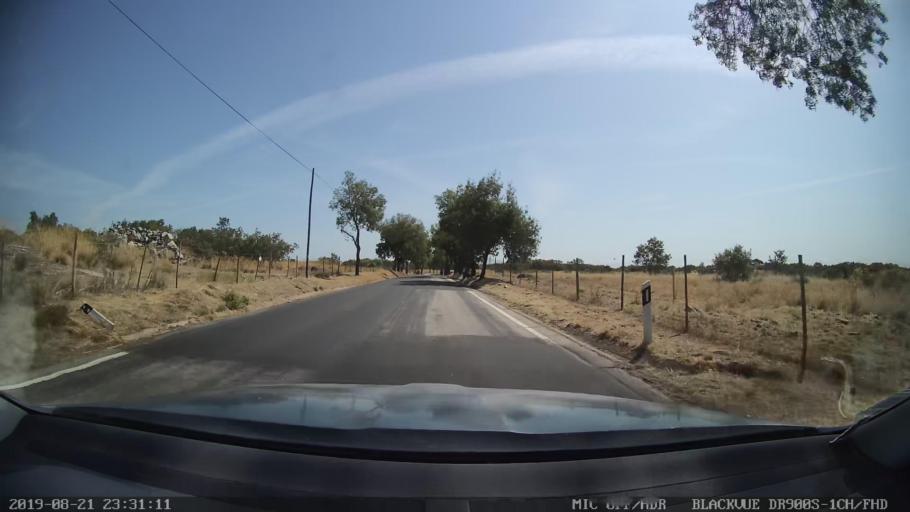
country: PT
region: Guarda
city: Alcains
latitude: 39.8718
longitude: -7.4339
